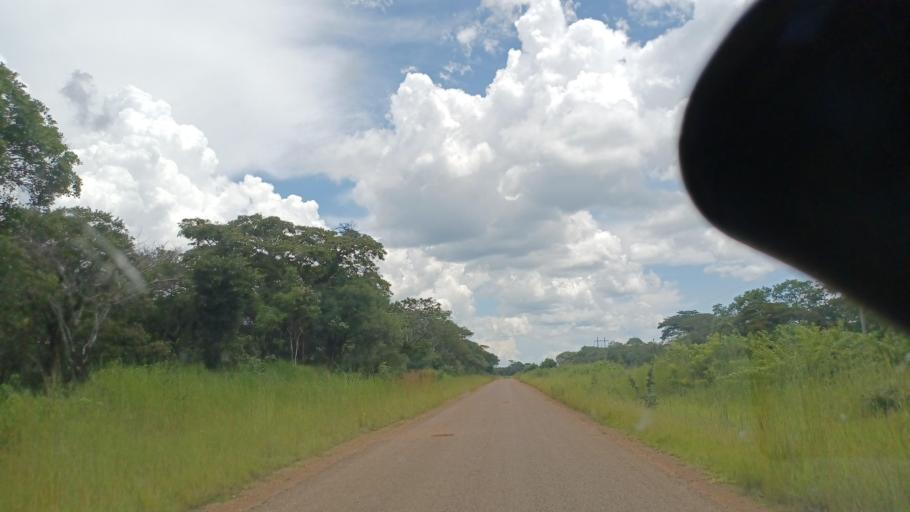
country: ZM
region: North-Western
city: Solwezi
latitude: -12.7124
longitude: 26.0248
